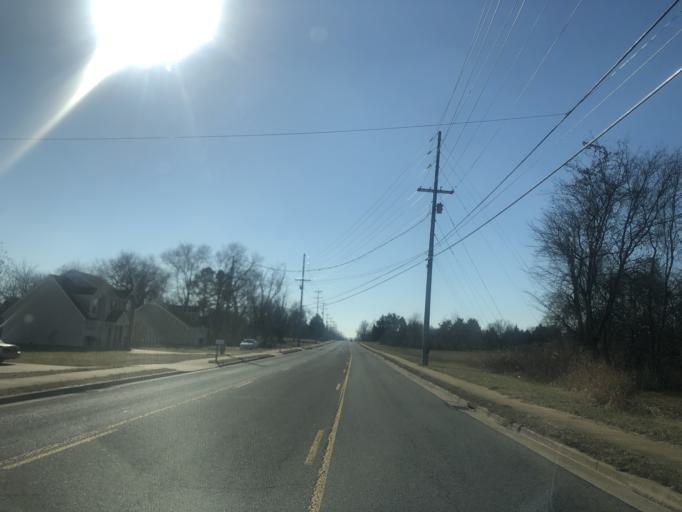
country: US
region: Tennessee
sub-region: Rutherford County
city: Smyrna
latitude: 35.9087
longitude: -86.4729
